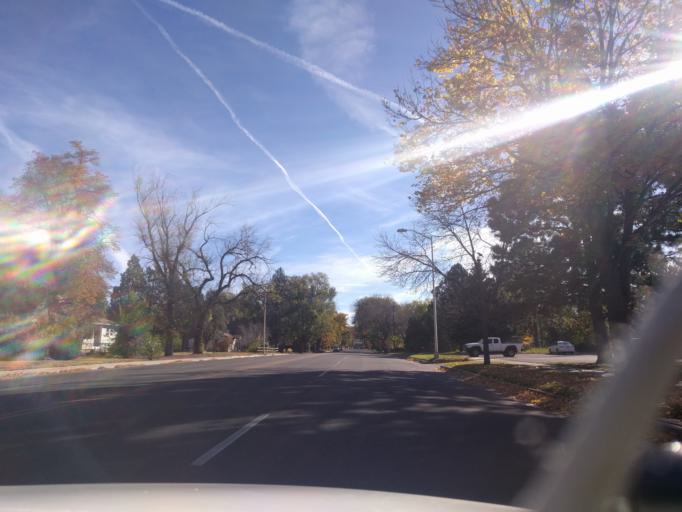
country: US
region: Colorado
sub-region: El Paso County
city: Colorado Springs
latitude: 38.8503
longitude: -104.8144
